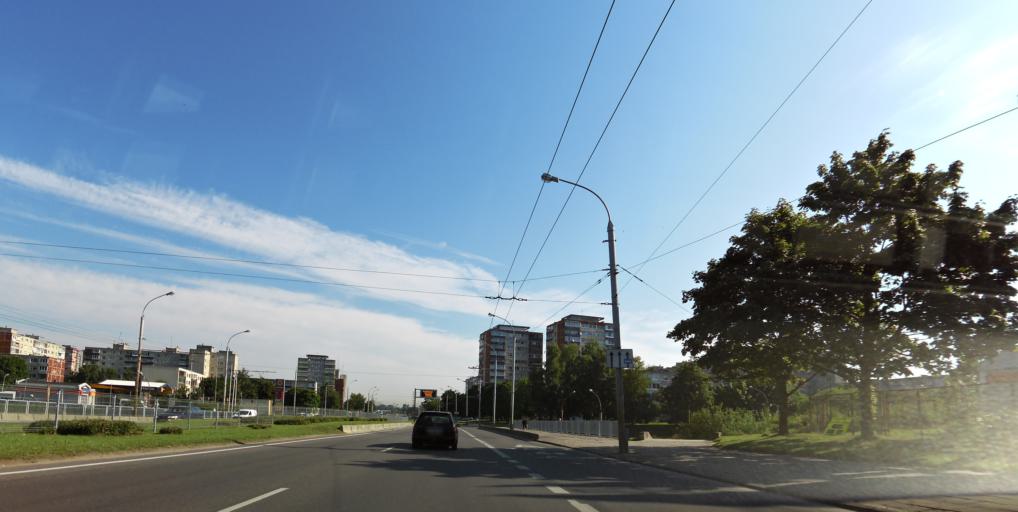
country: LT
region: Vilnius County
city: Justiniskes
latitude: 54.6939
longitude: 25.2184
